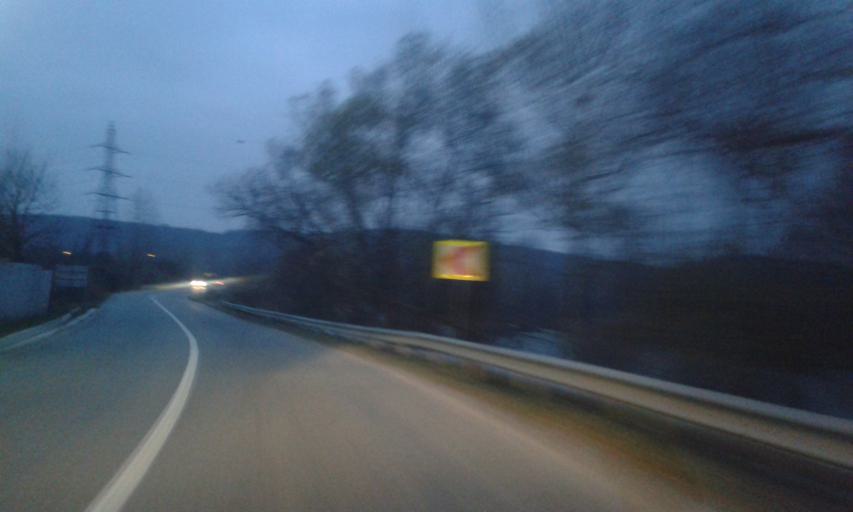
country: RO
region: Gorj
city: Targu Jiu
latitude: 45.0762
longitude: 23.2975
